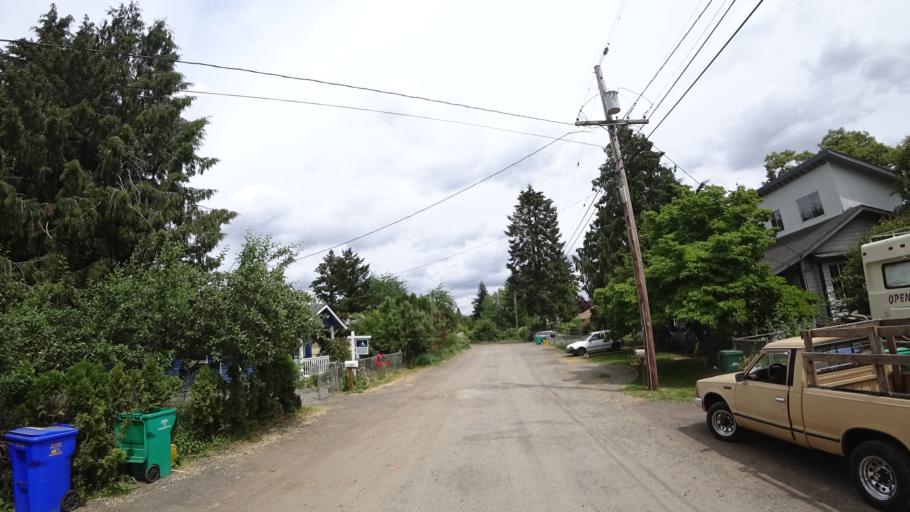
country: US
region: Oregon
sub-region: Multnomah County
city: Lents
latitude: 45.4866
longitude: -122.5541
